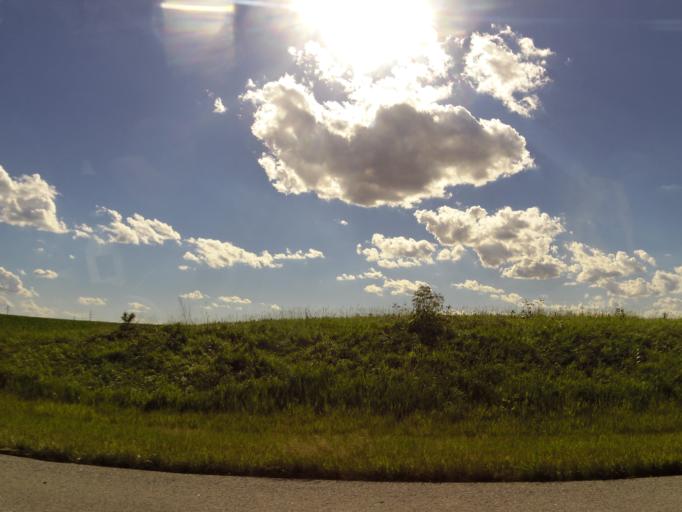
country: US
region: Missouri
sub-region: Lewis County
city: Canton
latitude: 40.0430
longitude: -91.5255
